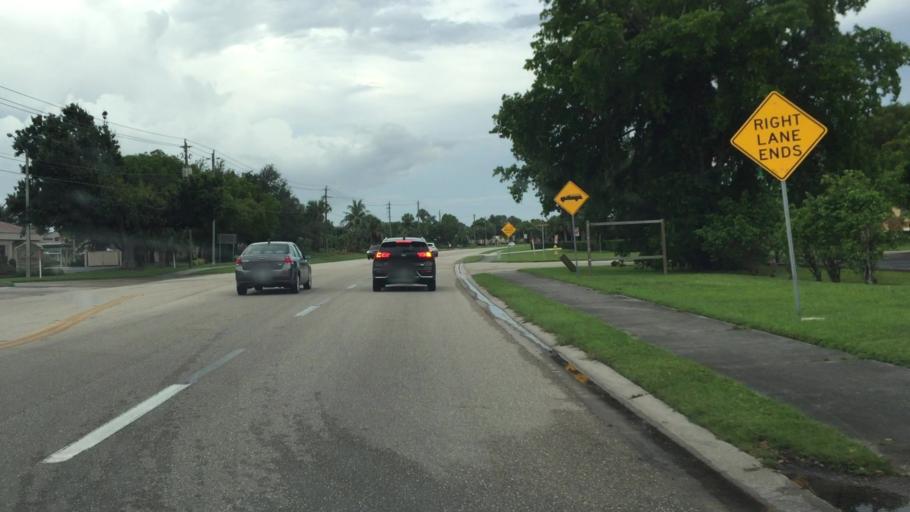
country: US
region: Florida
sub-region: Lee County
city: McGregor
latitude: 26.5558
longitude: -81.9041
